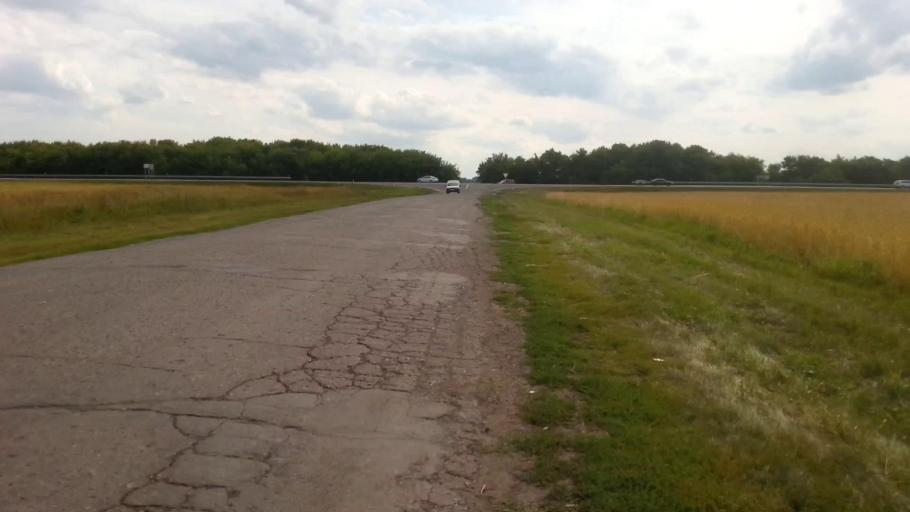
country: RU
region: Altai Krai
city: Nauchnyy Gorodok
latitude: 53.3580
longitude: 83.5083
